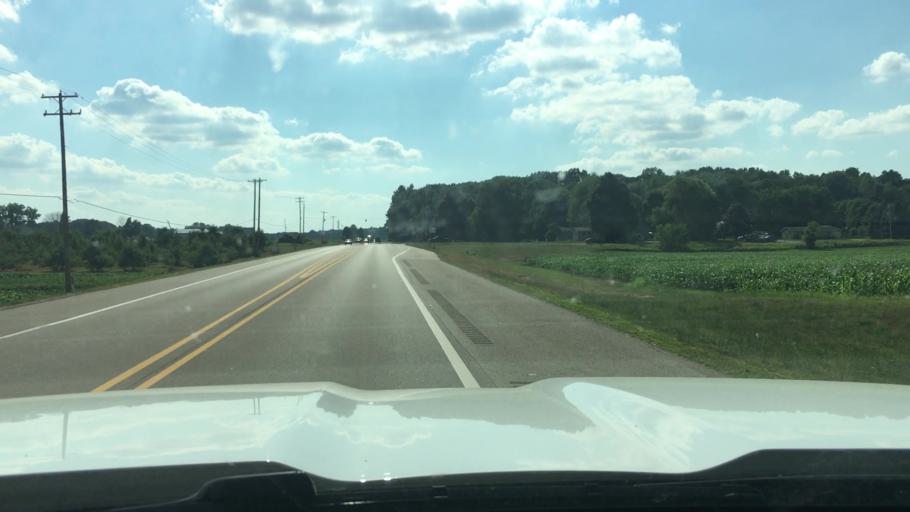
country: US
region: Michigan
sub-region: Kent County
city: Forest Hills
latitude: 43.0830
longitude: -85.3943
